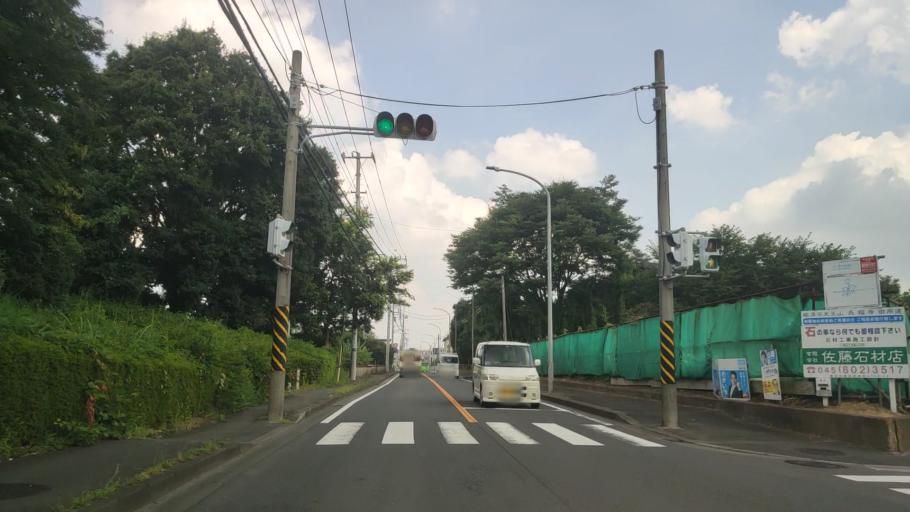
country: JP
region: Kanagawa
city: Minami-rinkan
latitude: 35.4544
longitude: 139.5018
